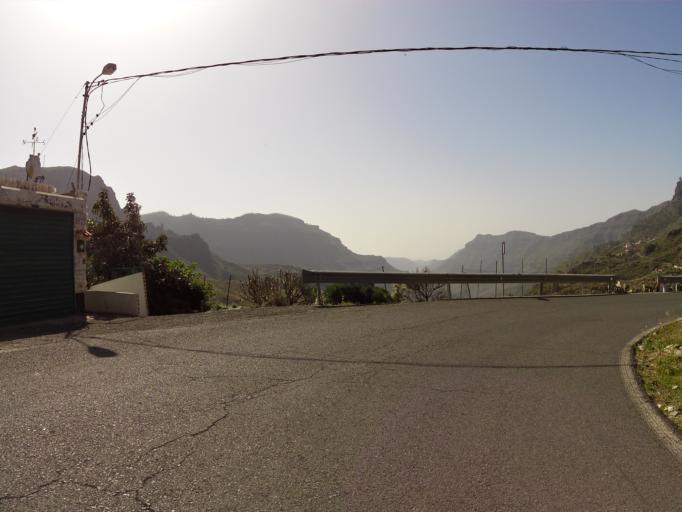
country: ES
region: Canary Islands
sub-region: Provincia de Las Palmas
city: Mogan
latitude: 27.9055
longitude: -15.6712
